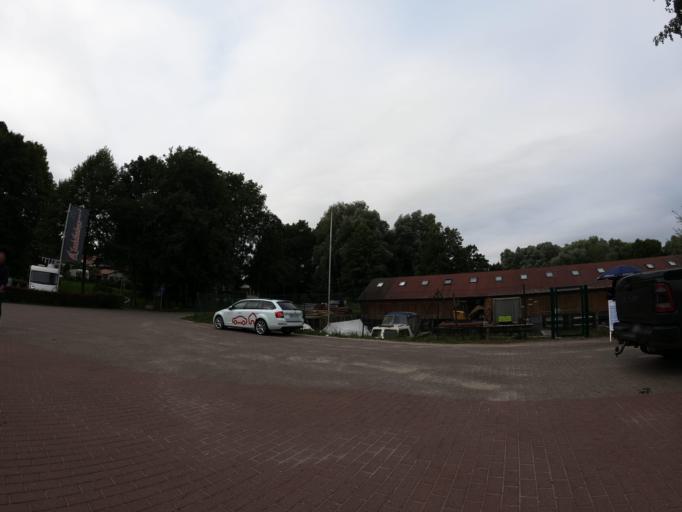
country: DE
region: Mecklenburg-Vorpommern
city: Malchow
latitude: 53.4915
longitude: 12.4803
